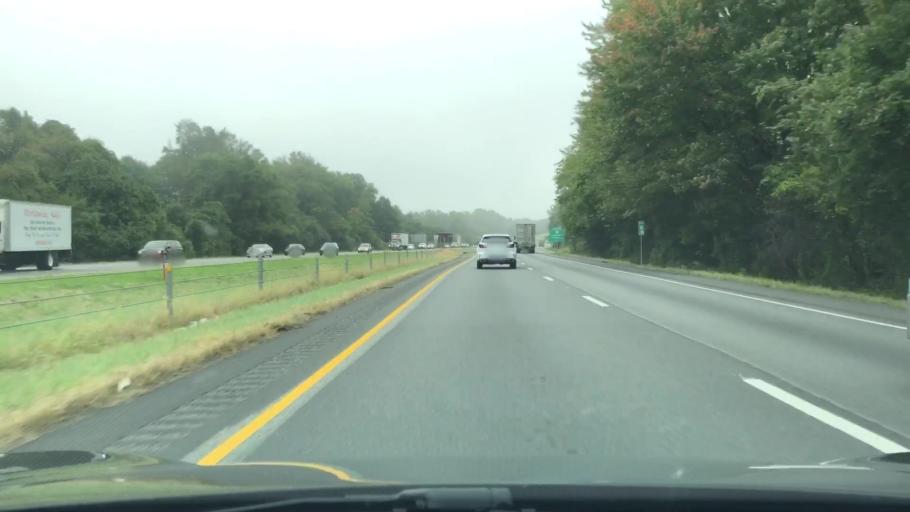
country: US
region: Pennsylvania
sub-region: Bucks County
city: Woodside
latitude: 40.2126
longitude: -74.8768
